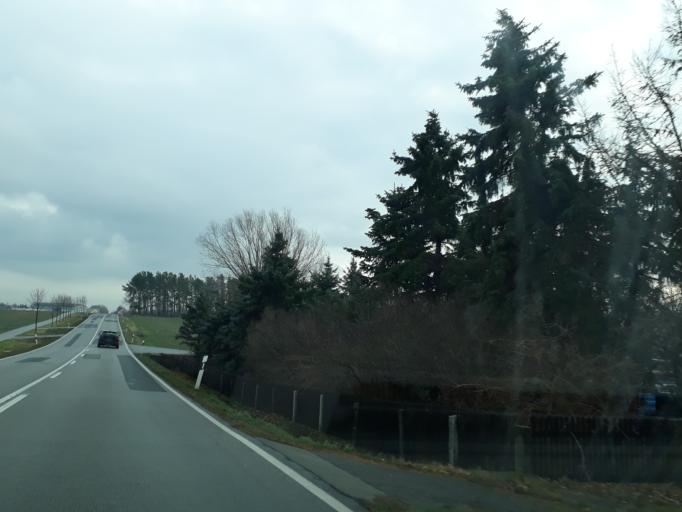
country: DE
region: Saxony
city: Kubschutz
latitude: 51.1668
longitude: 14.4952
